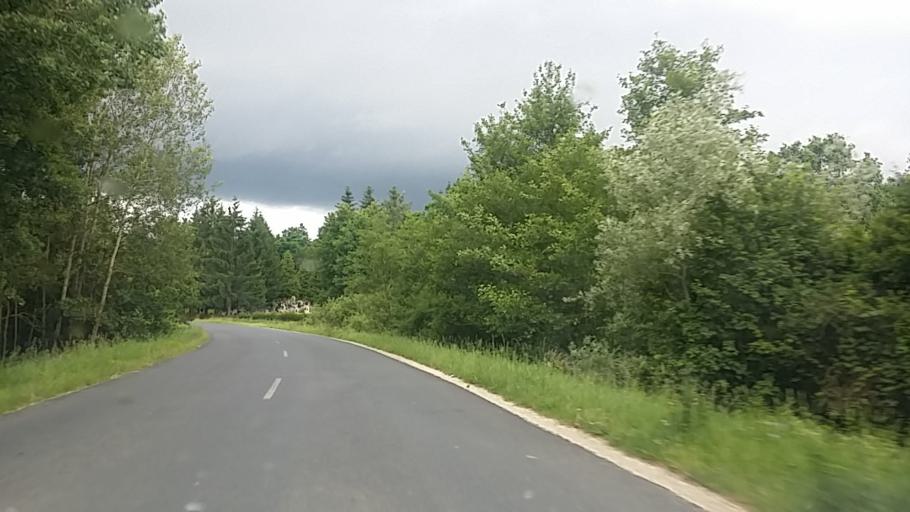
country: SI
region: Hodos-Hodos
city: Hodos
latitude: 46.8462
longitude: 16.4104
